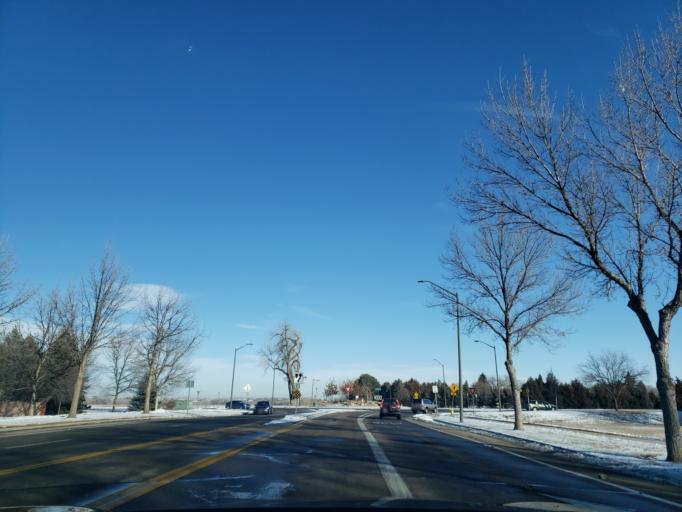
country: US
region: Colorado
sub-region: Larimer County
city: Fort Collins
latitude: 40.5378
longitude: -105.0214
